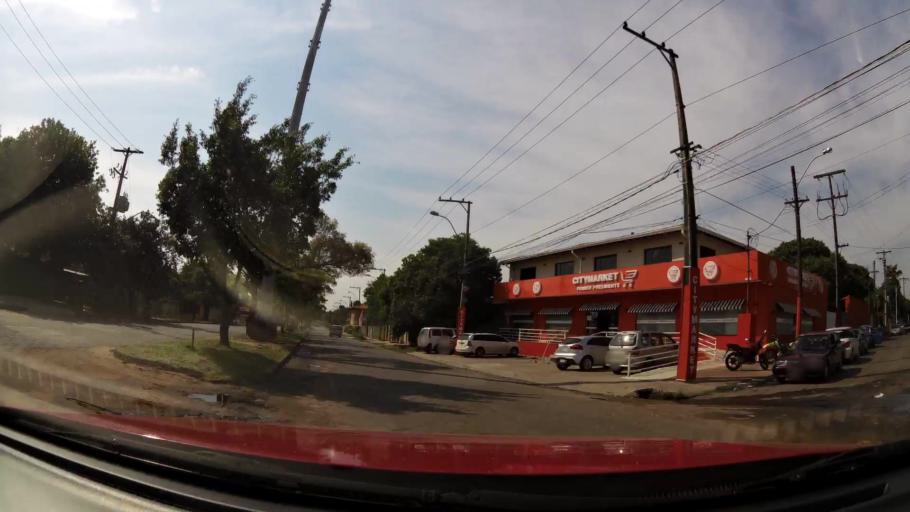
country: PY
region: Central
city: Fernando de la Mora
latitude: -25.2682
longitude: -57.5492
